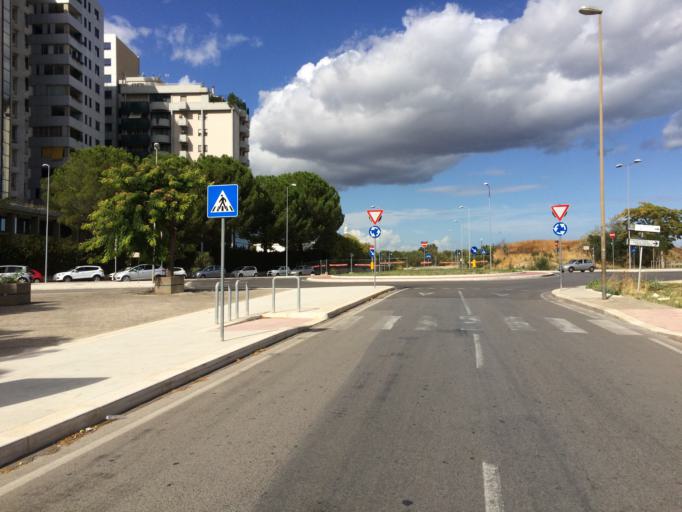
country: IT
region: Apulia
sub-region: Provincia di Bari
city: Bari
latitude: 41.0996
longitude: 16.8548
